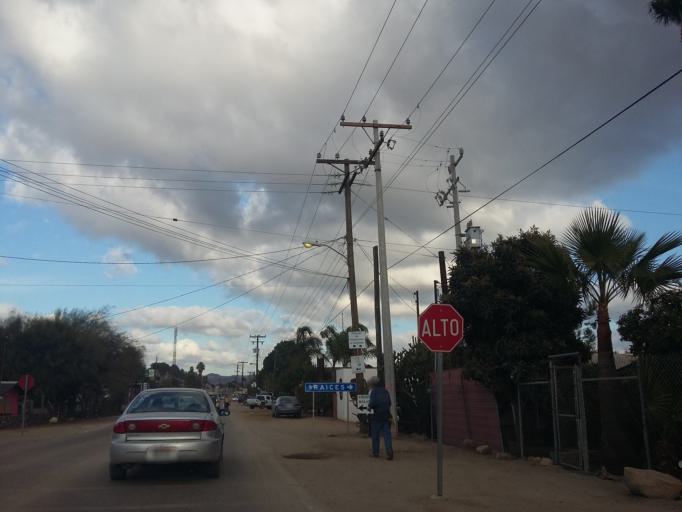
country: MX
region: Baja California
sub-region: Ensenada
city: Rancho Verde
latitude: 32.0955
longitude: -116.5728
